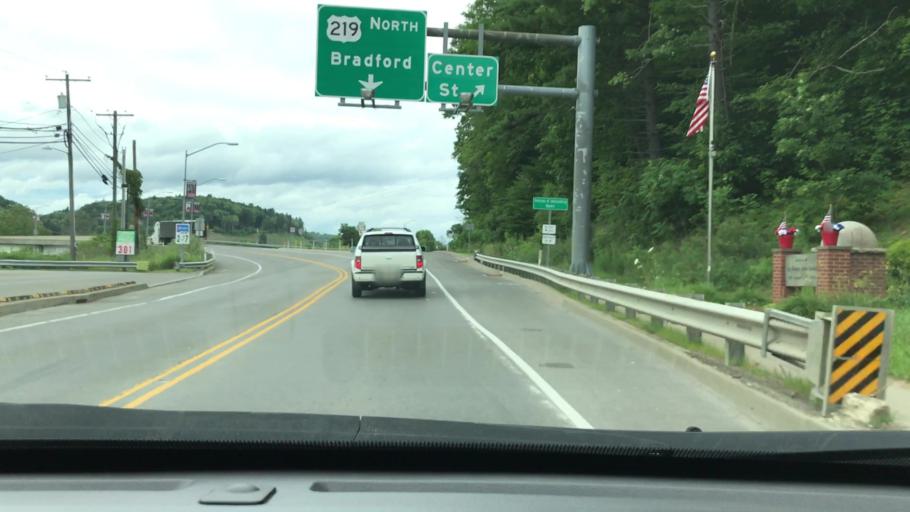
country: US
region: Pennsylvania
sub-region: Elk County
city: Johnsonburg
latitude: 41.4817
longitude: -78.6721
